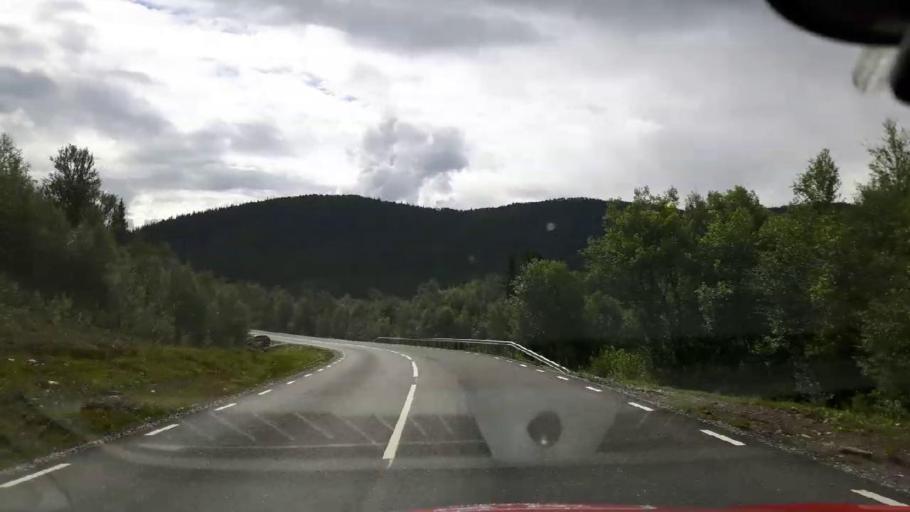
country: NO
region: Nord-Trondelag
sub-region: Royrvik
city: Royrvik
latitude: 64.8899
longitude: 14.1902
